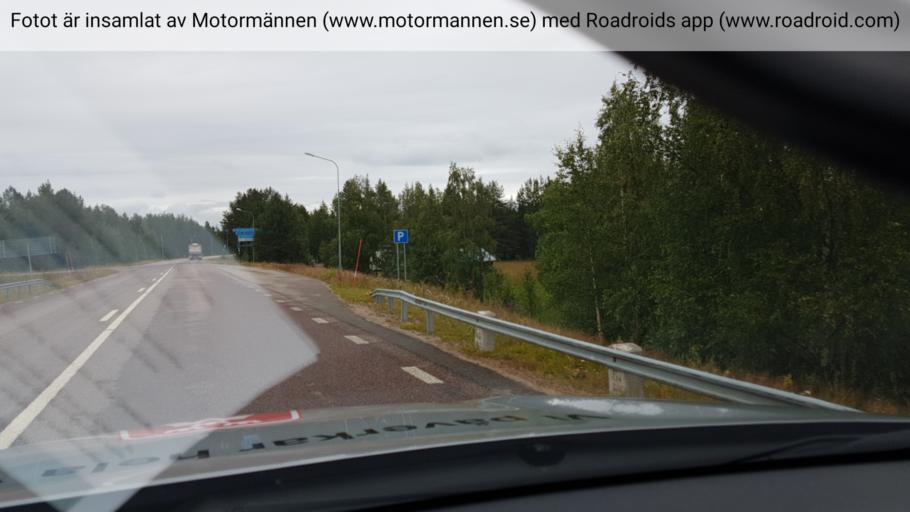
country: SE
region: Norrbotten
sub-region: Pajala Kommun
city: Pajala
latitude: 67.1602
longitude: 22.6313
